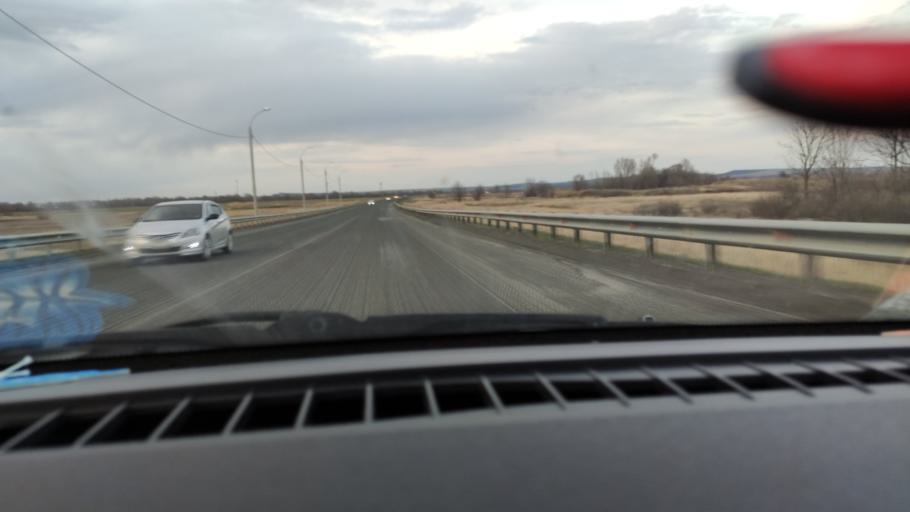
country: RU
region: Saratov
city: Yelshanka
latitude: 51.8092
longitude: 46.1986
